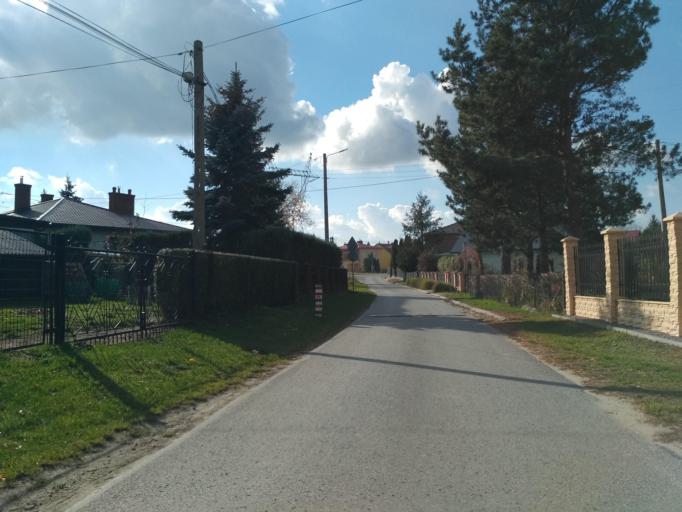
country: PL
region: Subcarpathian Voivodeship
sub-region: Powiat rzeszowski
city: Swilcza
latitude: 50.1180
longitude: 21.8837
